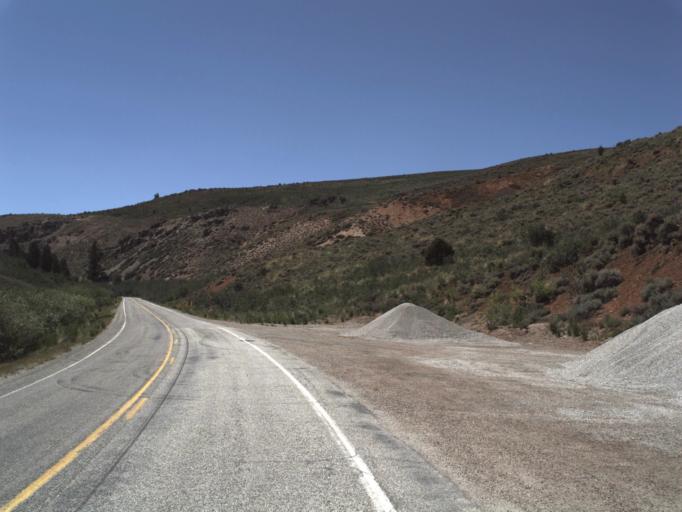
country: US
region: Utah
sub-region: Rich County
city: Randolph
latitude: 41.4805
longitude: -111.3704
